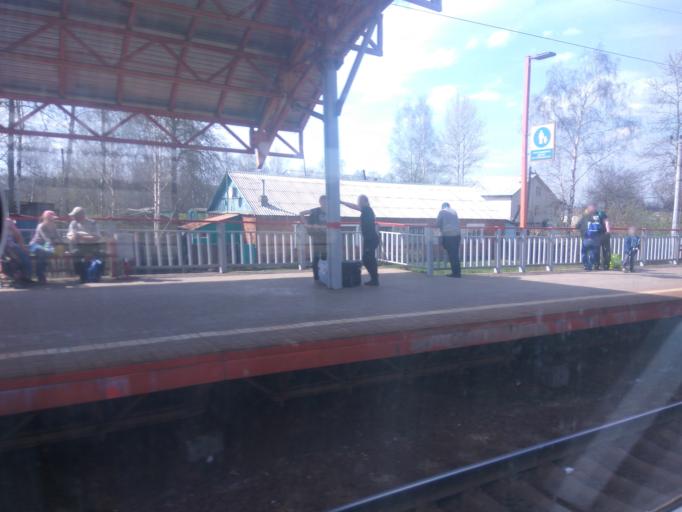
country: RU
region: Moskovskaya
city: Podosinki
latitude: 56.2067
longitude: 37.5261
